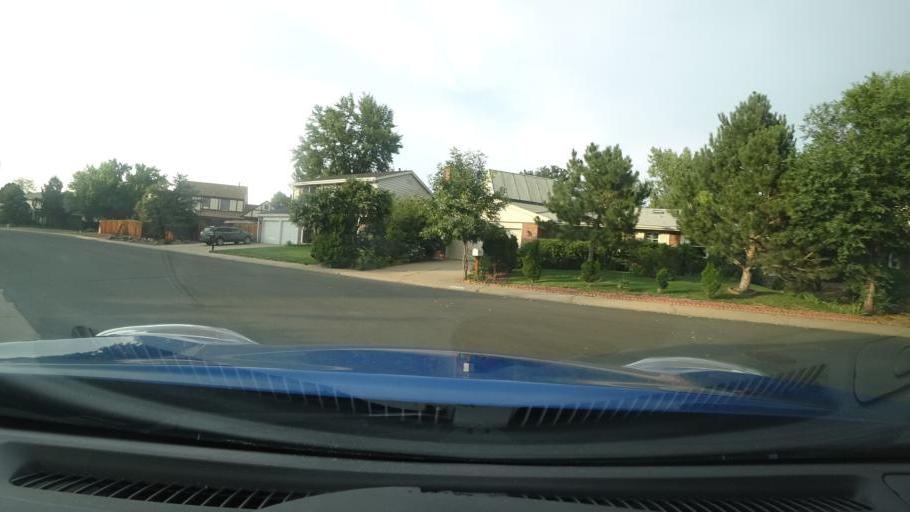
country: US
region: Colorado
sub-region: Adams County
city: Aurora
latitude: 39.6912
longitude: -104.8220
